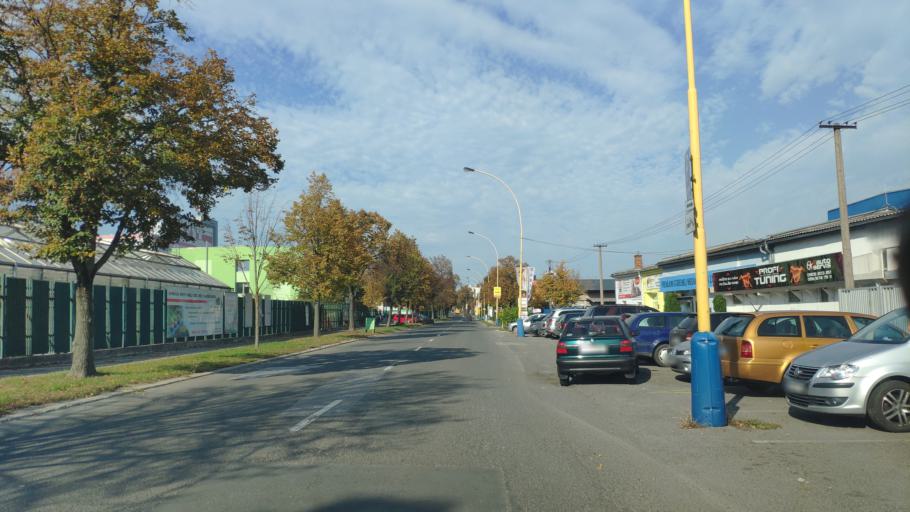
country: SK
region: Kosicky
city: Kosice
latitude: 48.6962
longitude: 21.2620
